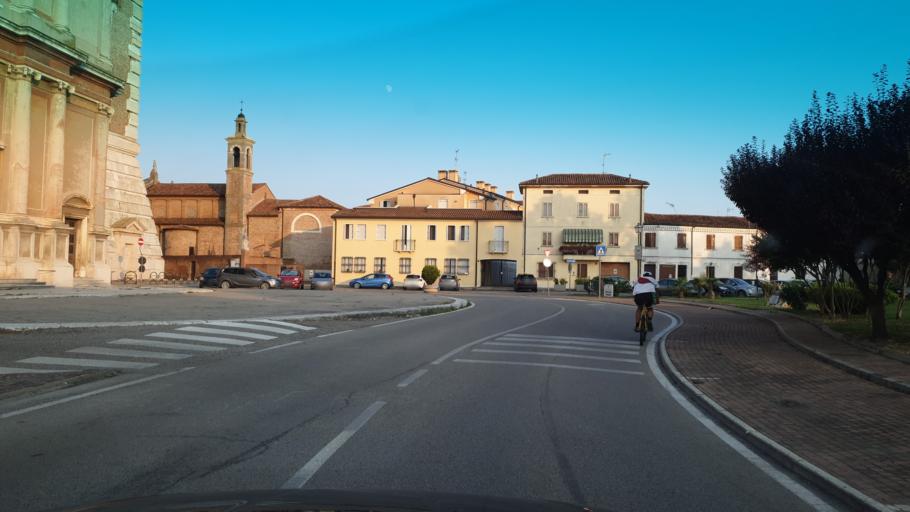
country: IT
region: Veneto
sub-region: Provincia di Rovigo
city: Lendinara
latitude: 45.0848
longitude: 11.6028
